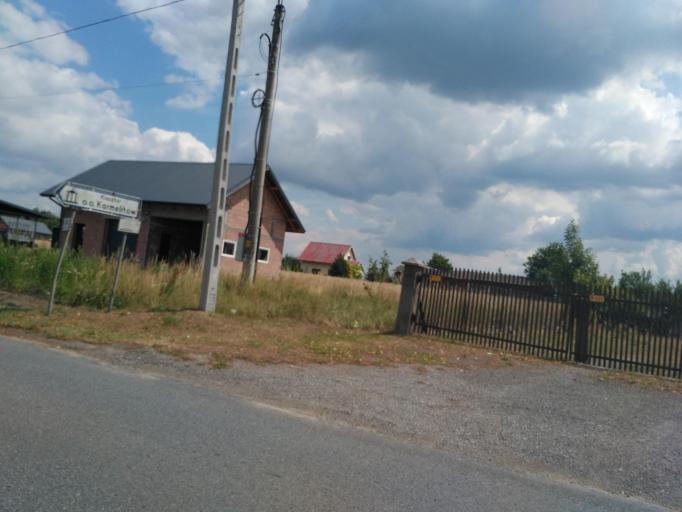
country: PL
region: Subcarpathian Voivodeship
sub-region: Powiat debicki
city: Pilzno
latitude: 50.0165
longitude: 21.2901
